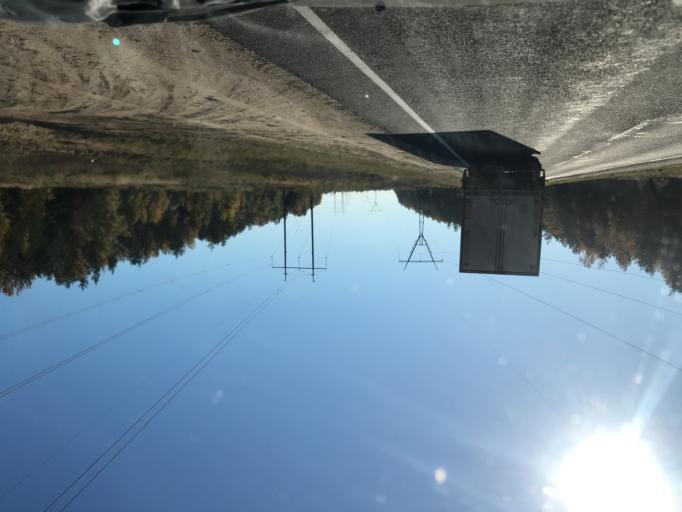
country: BY
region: Mogilev
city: Babruysk
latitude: 53.1140
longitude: 29.0541
